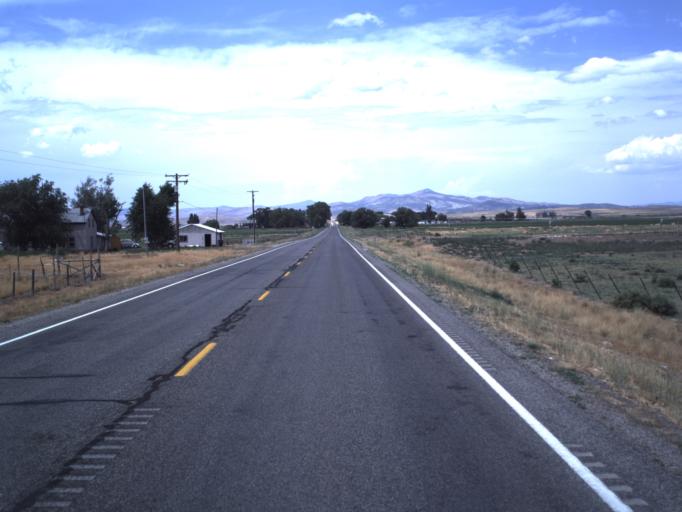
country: US
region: Utah
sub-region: Sanpete County
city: Moroni
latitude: 39.4636
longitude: -111.5627
